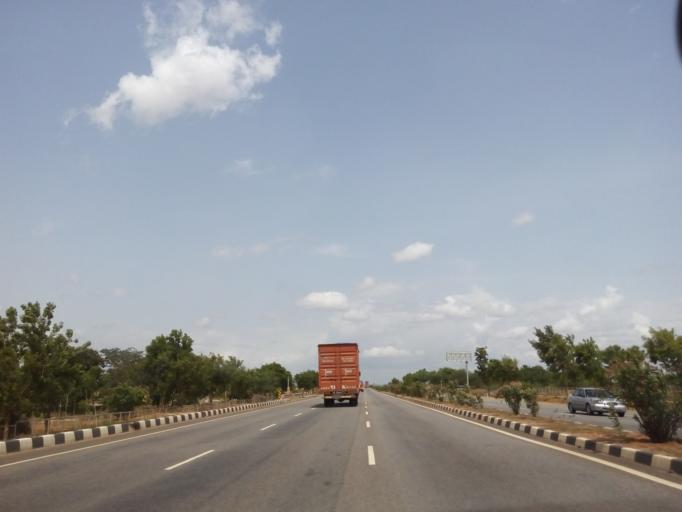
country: IN
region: Karnataka
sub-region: Tumkur
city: Sira
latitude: 13.7304
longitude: 76.8961
